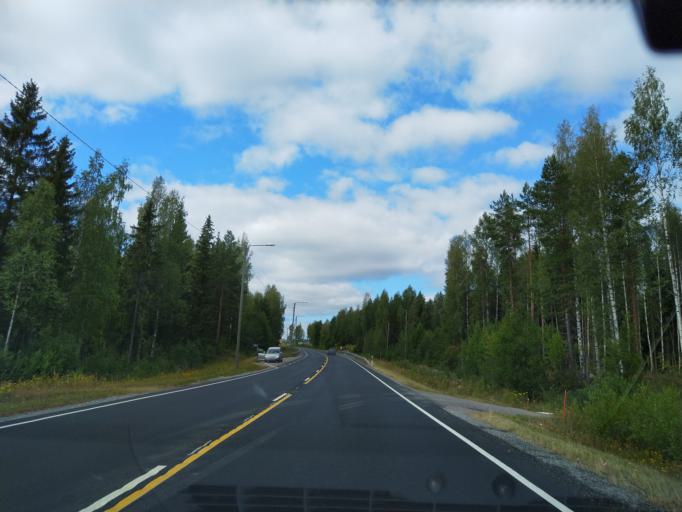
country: FI
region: Haeme
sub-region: Riihimaeki
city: Loppi
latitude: 60.7192
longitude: 24.4603
